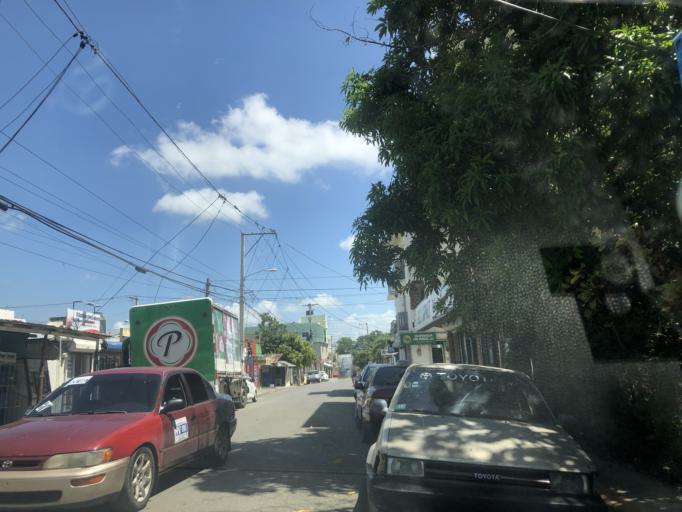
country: DO
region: Santiago
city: La Canela
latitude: 19.4512
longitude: -70.7819
